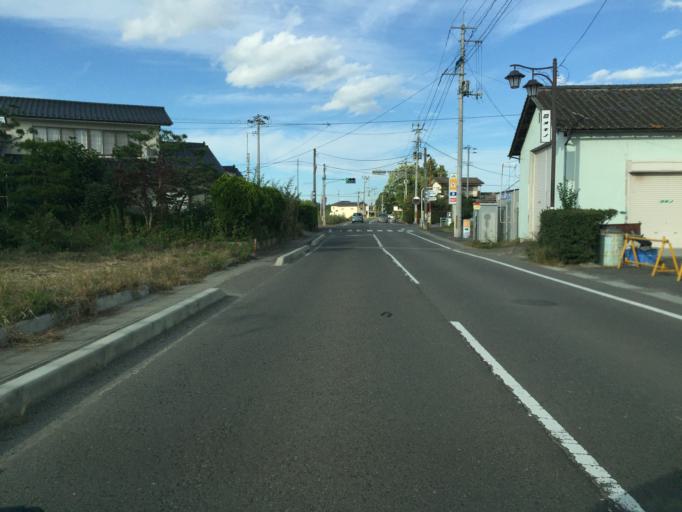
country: JP
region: Fukushima
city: Fukushima-shi
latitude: 37.7114
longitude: 140.4345
